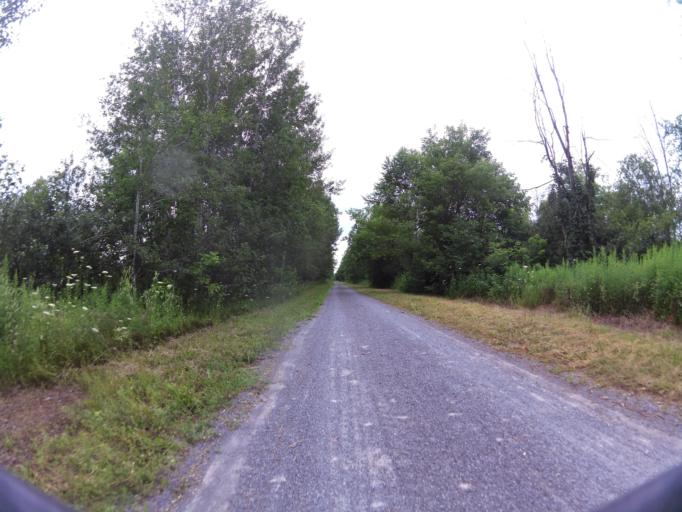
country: CA
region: Ontario
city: Ottawa
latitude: 45.2610
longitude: -75.6228
